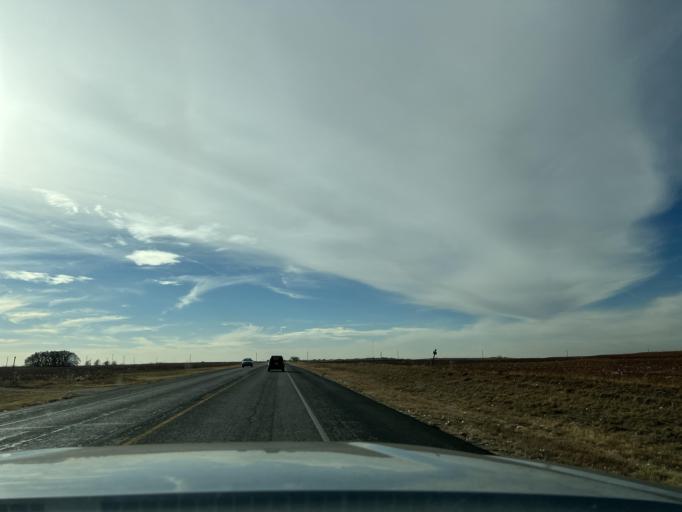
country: US
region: Texas
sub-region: Fisher County
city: Roby
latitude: 32.7524
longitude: -100.3427
